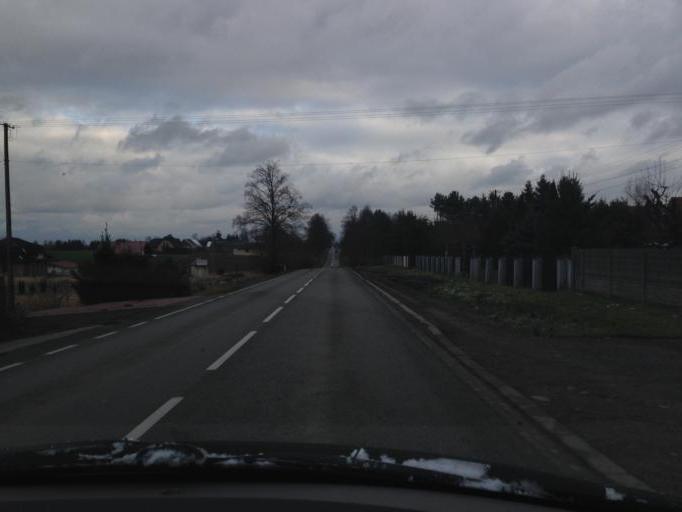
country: PL
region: Lesser Poland Voivodeship
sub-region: Powiat wielicki
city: Gdow
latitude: 49.9071
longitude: 20.1728
